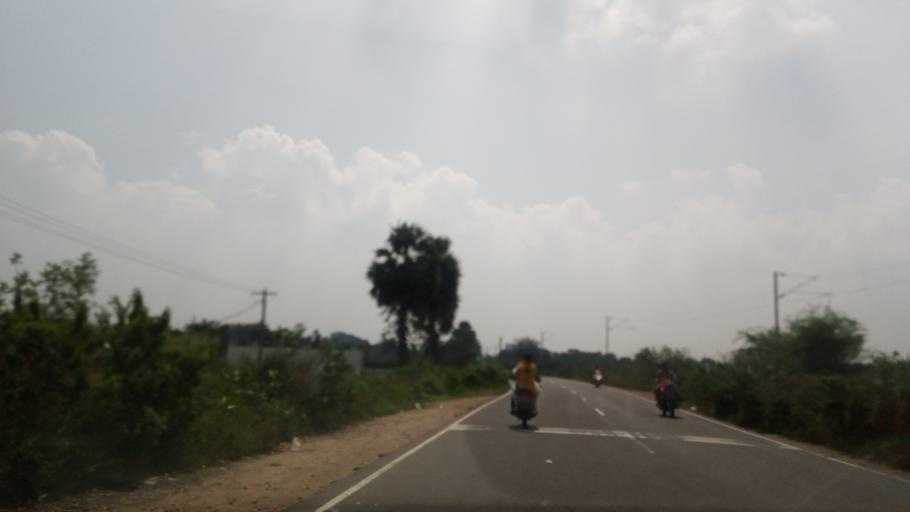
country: IN
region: Tamil Nadu
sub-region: Kancheepuram
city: Kanchipuram
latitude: 12.8852
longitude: 79.6881
